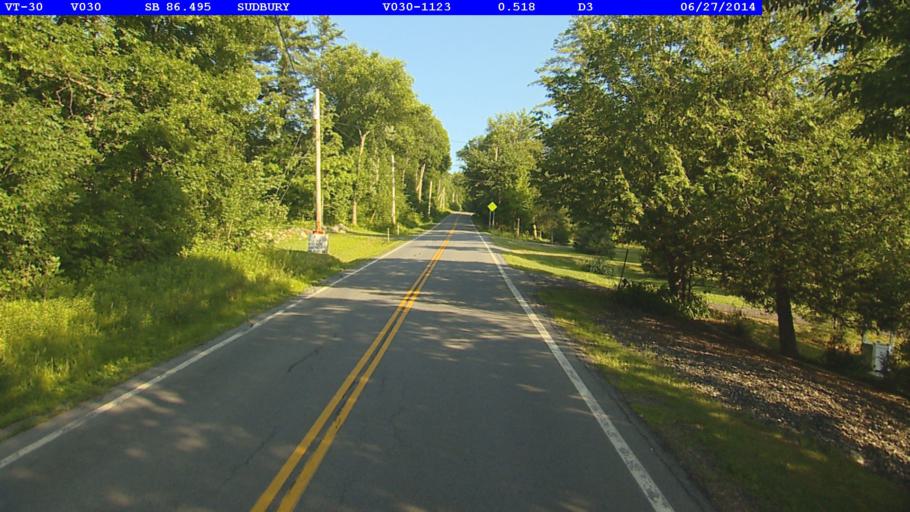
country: US
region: Vermont
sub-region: Rutland County
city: Brandon
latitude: 43.7570
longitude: -73.1933
